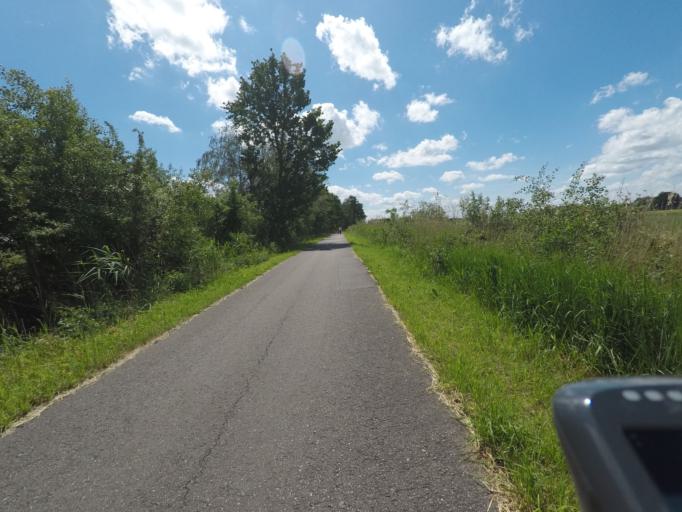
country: DE
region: Hamburg
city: Bergedorf
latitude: 53.4356
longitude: 10.2112
